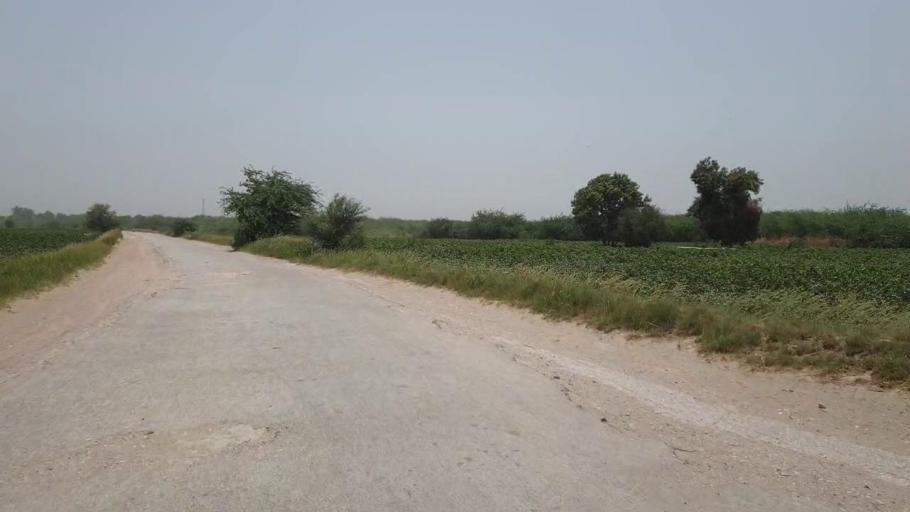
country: PK
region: Sindh
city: Tando Mittha Khan
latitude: 26.0675
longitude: 69.1999
